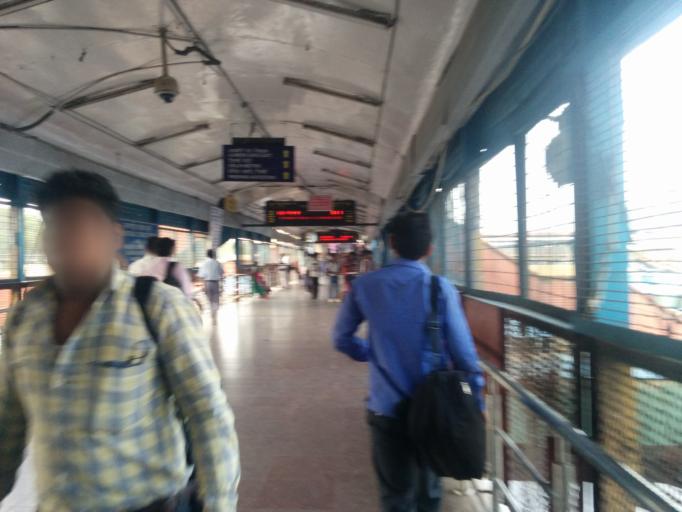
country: IN
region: NCT
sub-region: New Delhi
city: New Delhi
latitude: 28.6435
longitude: 77.2192
